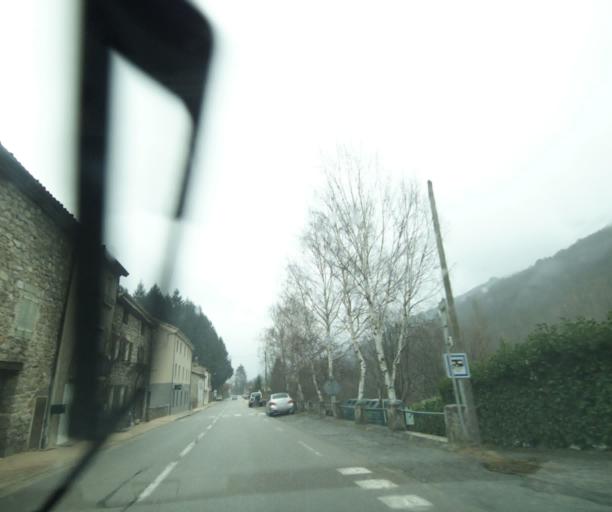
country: FR
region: Rhone-Alpes
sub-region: Departement de l'Ardeche
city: Thueyts
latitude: 44.6684
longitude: 4.1703
